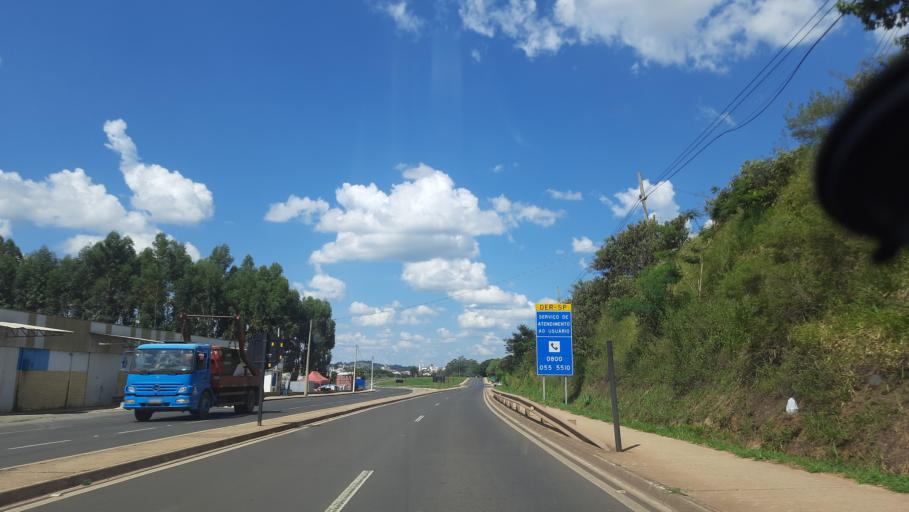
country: BR
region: Sao Paulo
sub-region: Sao Jose Do Rio Pardo
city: Sao Jose do Rio Pardo
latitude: -21.6029
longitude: -46.9134
